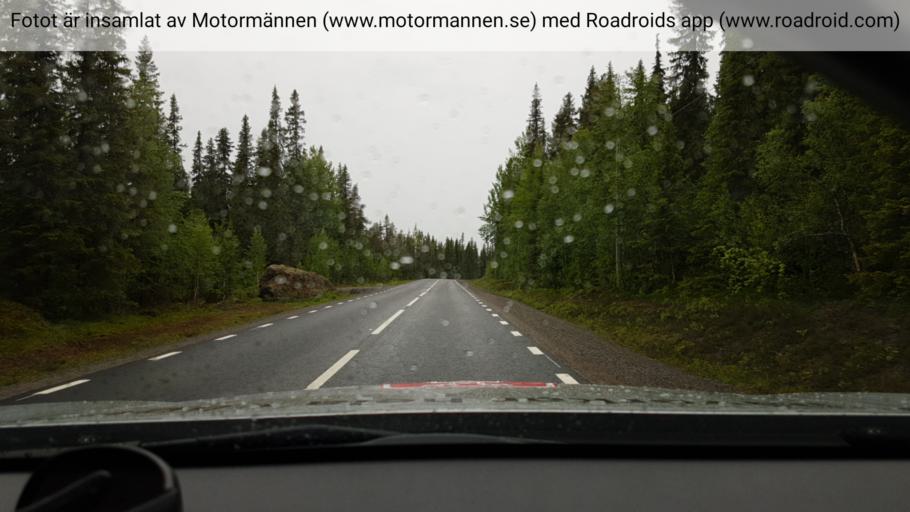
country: SE
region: Vaesterbotten
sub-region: Storumans Kommun
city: Fristad
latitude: 65.8150
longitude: 16.8643
